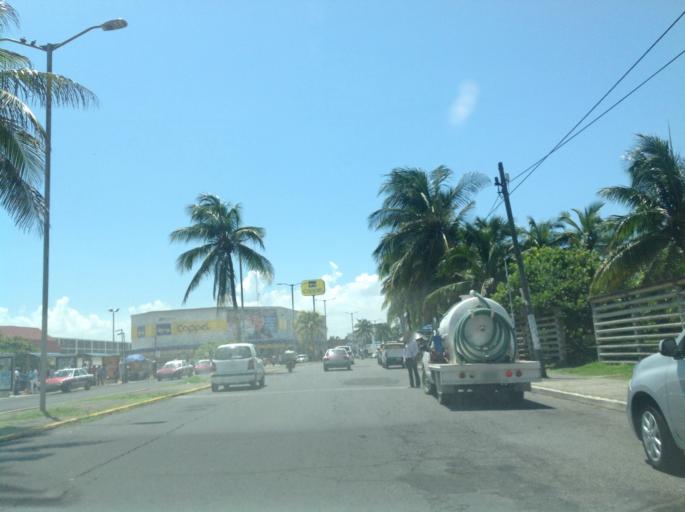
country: MX
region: Veracruz
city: Veracruz
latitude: 19.1597
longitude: -96.1104
